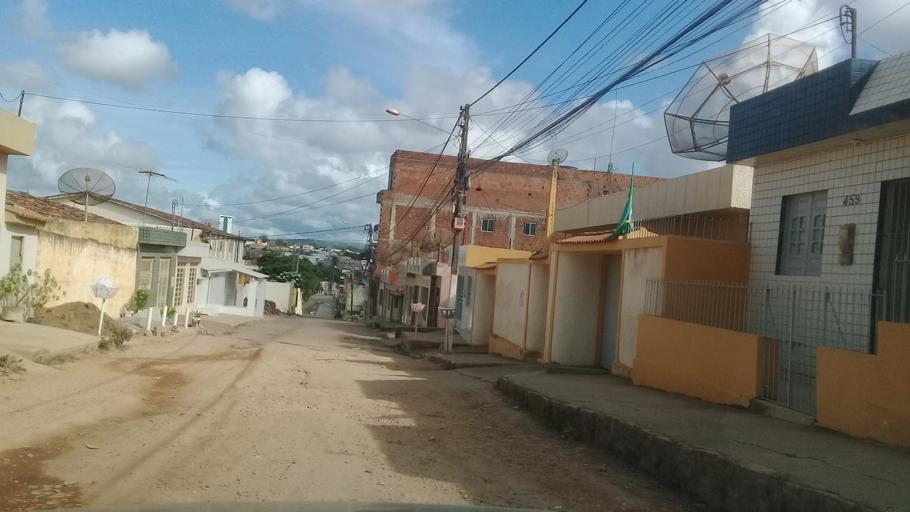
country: BR
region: Pernambuco
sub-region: Vitoria De Santo Antao
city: Vitoria de Santo Antao
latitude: -8.1300
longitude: -35.2933
